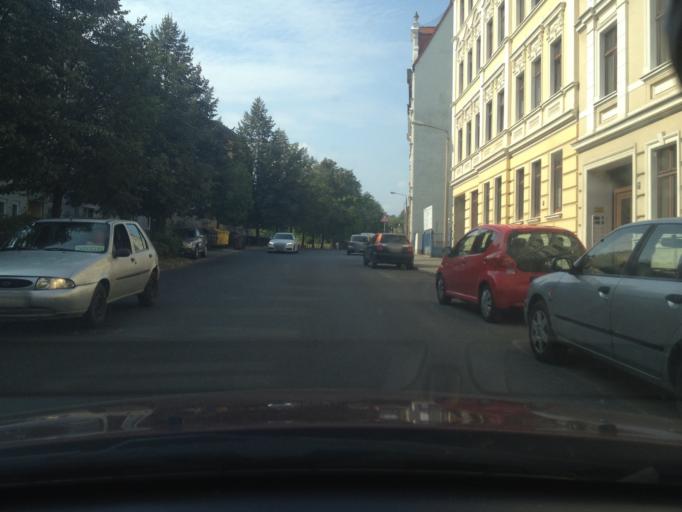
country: DE
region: Saxony
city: Goerlitz
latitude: 51.1589
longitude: 14.9807
